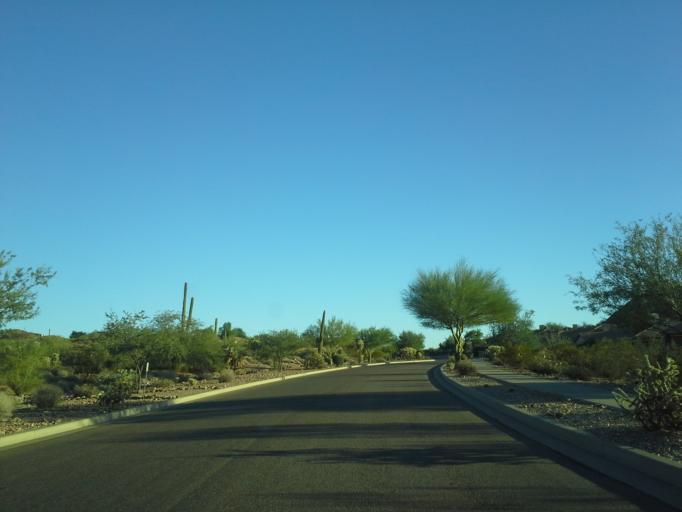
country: US
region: Arizona
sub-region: Pinal County
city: Apache Junction
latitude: 33.3743
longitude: -111.4611
